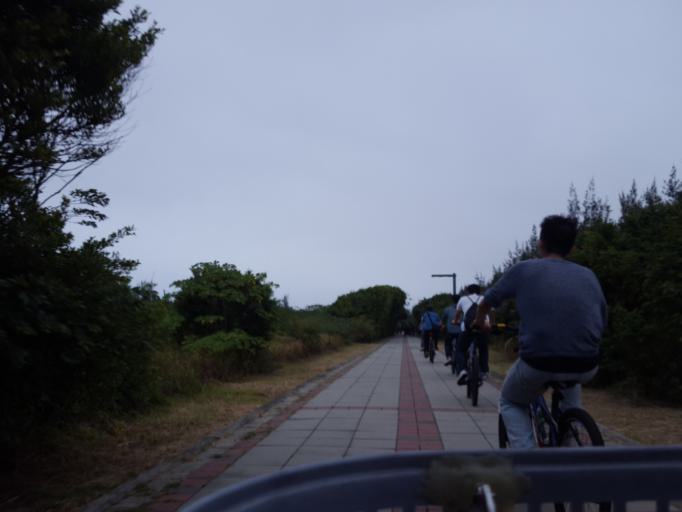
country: TW
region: Taiwan
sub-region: Hsinchu
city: Hsinchu
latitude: 24.8403
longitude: 120.9204
